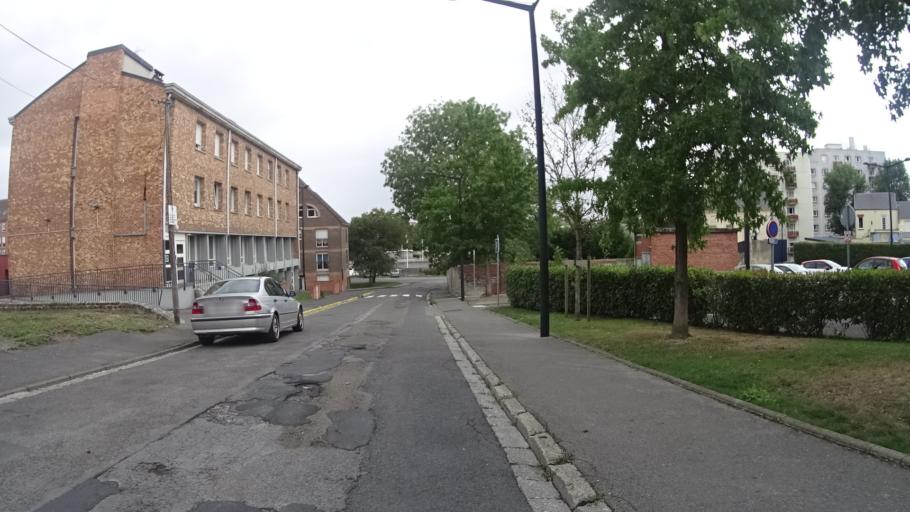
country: FR
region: Nord-Pas-de-Calais
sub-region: Departement du Nord
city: Hautmont
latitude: 50.2489
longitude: 3.9167
